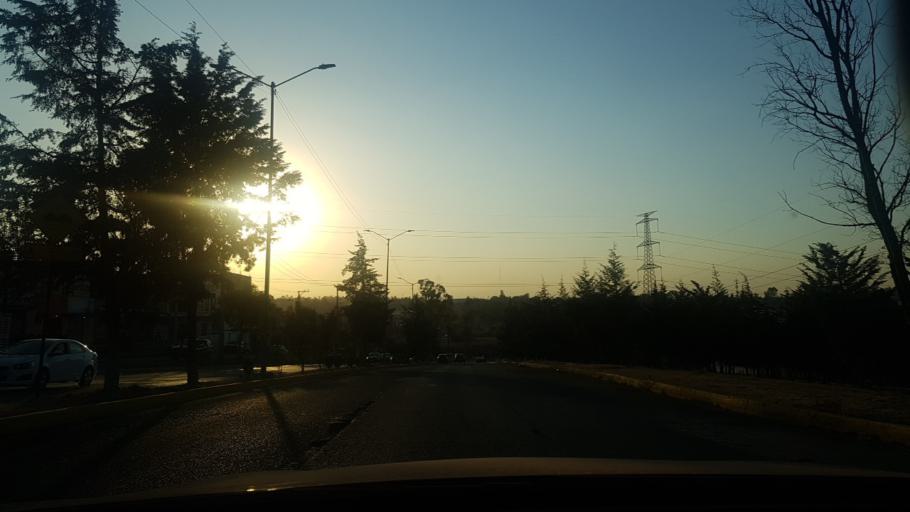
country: MX
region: Mexico
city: Cuautitlan Izcalli
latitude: 19.6360
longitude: -99.2172
